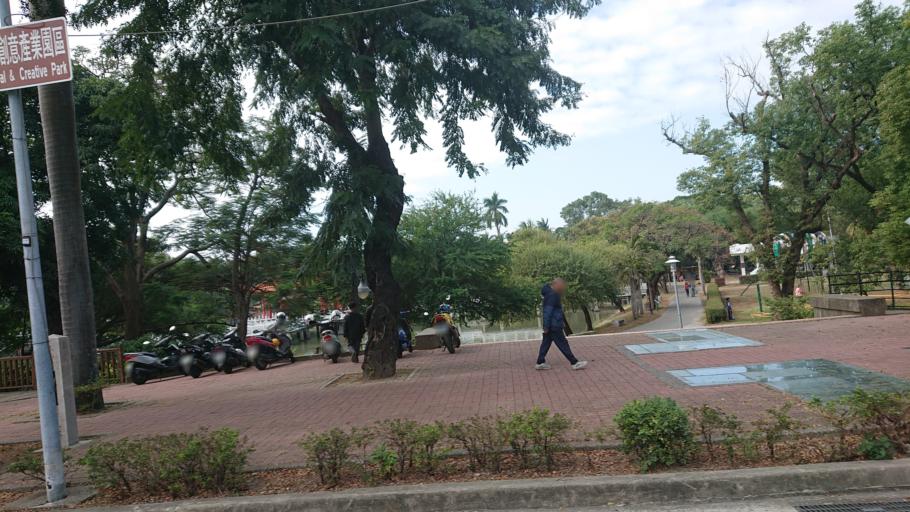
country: TW
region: Taiwan
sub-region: Tainan
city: Tainan
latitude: 23.0017
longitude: 120.2130
